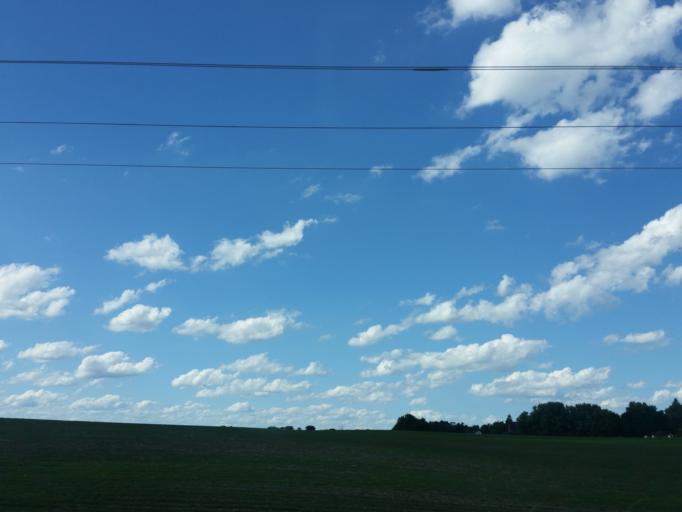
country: US
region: Minnesota
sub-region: Wright County
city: Cokato
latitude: 45.0659
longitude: -94.2183
